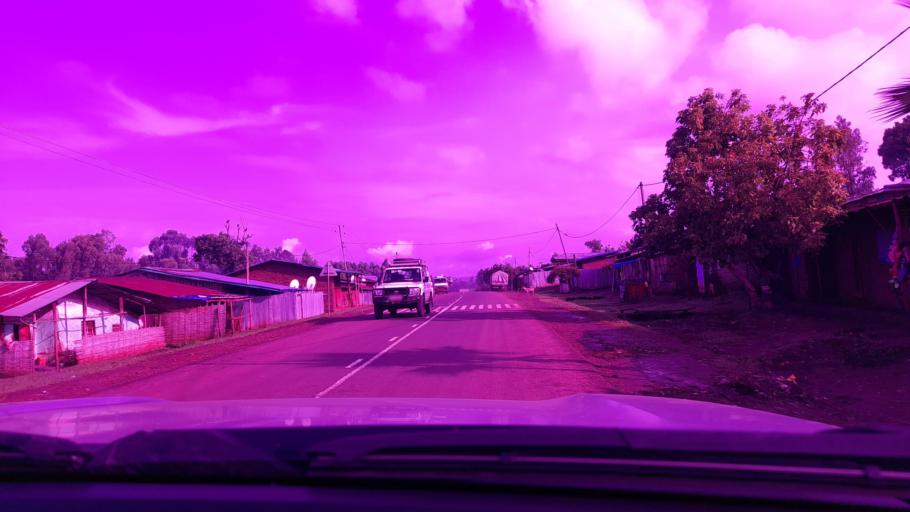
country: ET
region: Oromiya
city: Bedele
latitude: 8.1751
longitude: 36.4588
